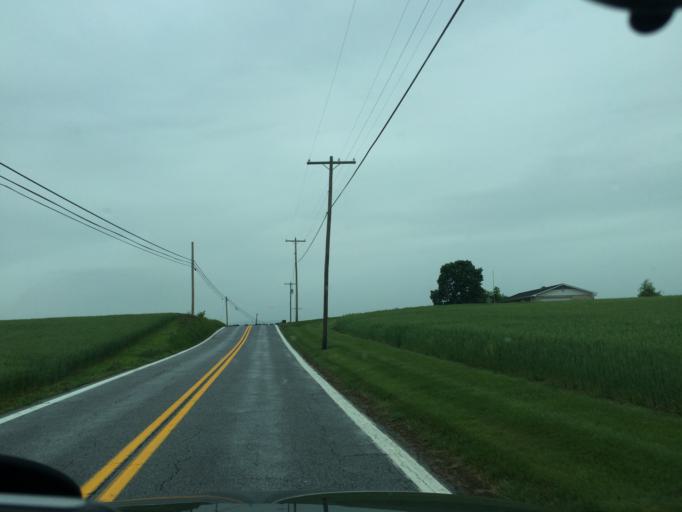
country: US
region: Maryland
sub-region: Carroll County
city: Taneytown
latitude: 39.6048
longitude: -77.2473
